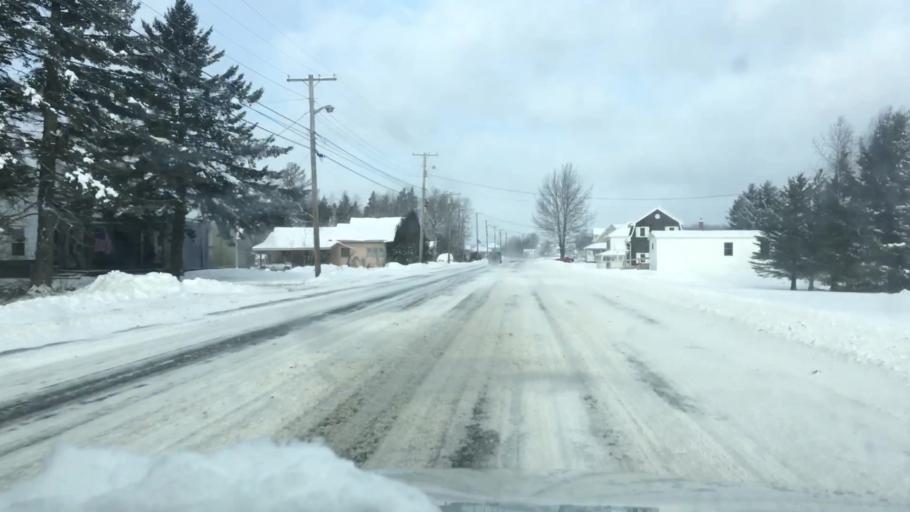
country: US
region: Maine
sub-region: Aroostook County
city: Van Buren
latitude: 47.1817
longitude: -67.9527
